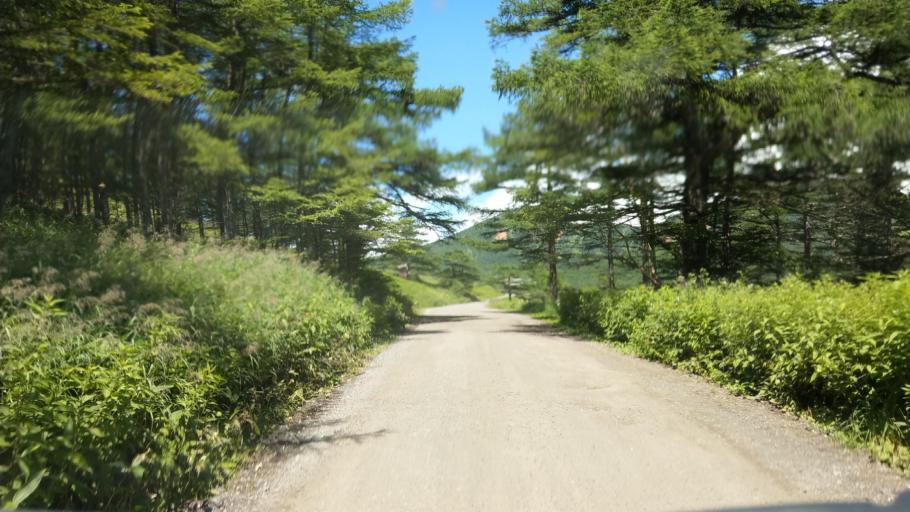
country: JP
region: Nagano
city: Komoro
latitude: 36.4060
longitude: 138.4668
